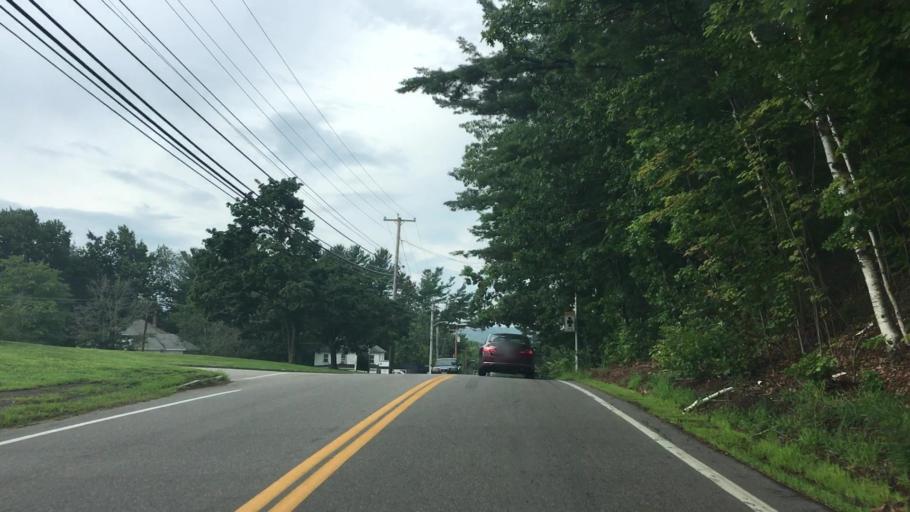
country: US
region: Maine
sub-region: York County
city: Sanford (historical)
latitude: 43.4494
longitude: -70.7688
